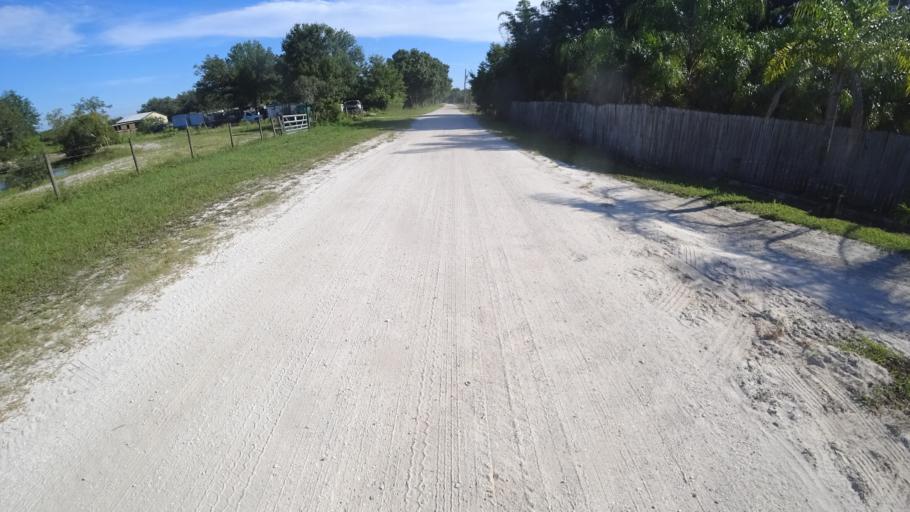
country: US
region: Florida
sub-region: Sarasota County
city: Lake Sarasota
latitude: 27.4099
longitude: -82.2567
